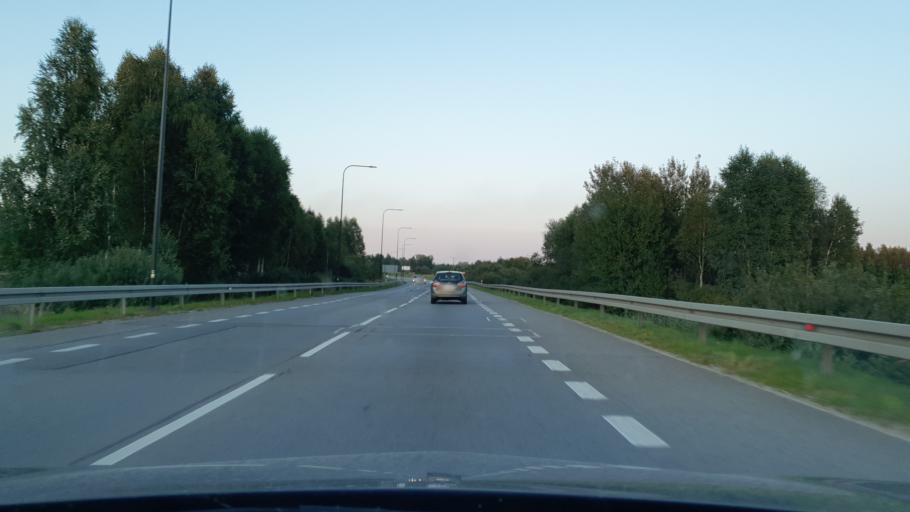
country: PL
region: Pomeranian Voivodeship
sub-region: Powiat leborski
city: Lebork
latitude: 54.5400
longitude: 17.7799
